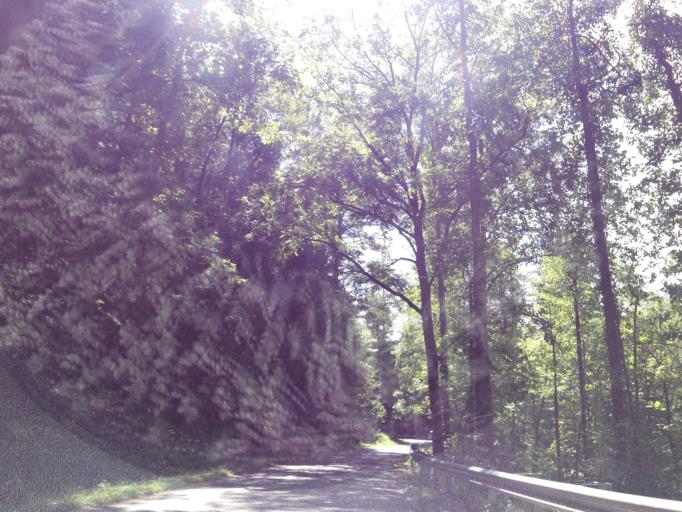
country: US
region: Tennessee
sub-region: Roane County
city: Rockwood
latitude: 35.8915
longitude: -84.7797
